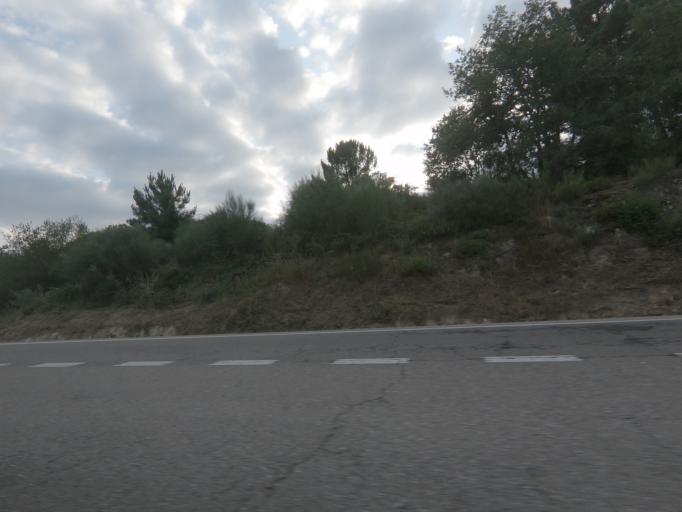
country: ES
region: Galicia
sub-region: Provincia de Ourense
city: Taboadela
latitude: 42.2292
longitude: -7.8431
